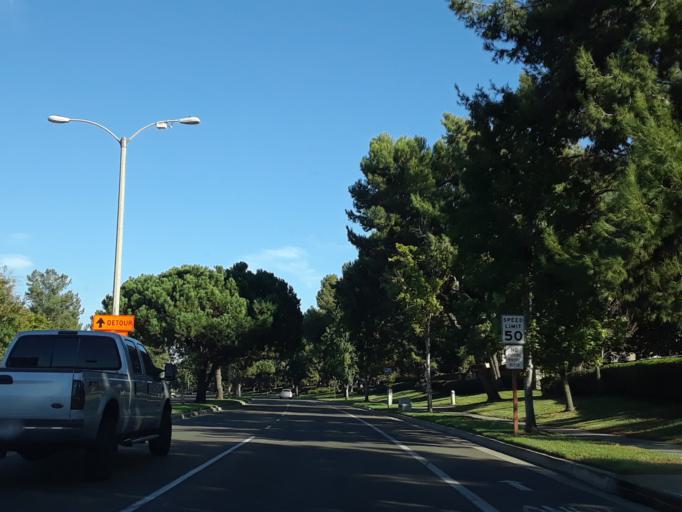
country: US
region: California
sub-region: Orange County
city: Irvine
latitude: 33.6731
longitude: -117.8002
